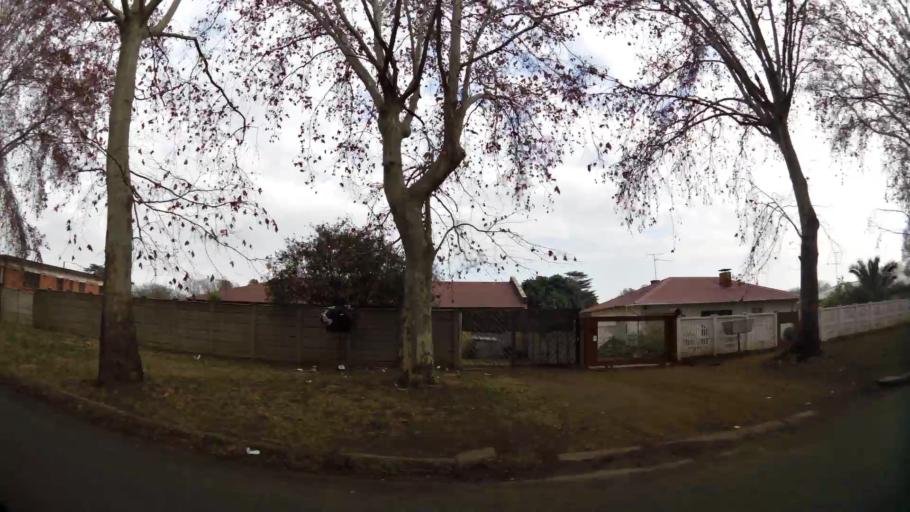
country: ZA
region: Gauteng
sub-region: Sedibeng District Municipality
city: Vanderbijlpark
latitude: -26.6850
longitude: 27.8162
